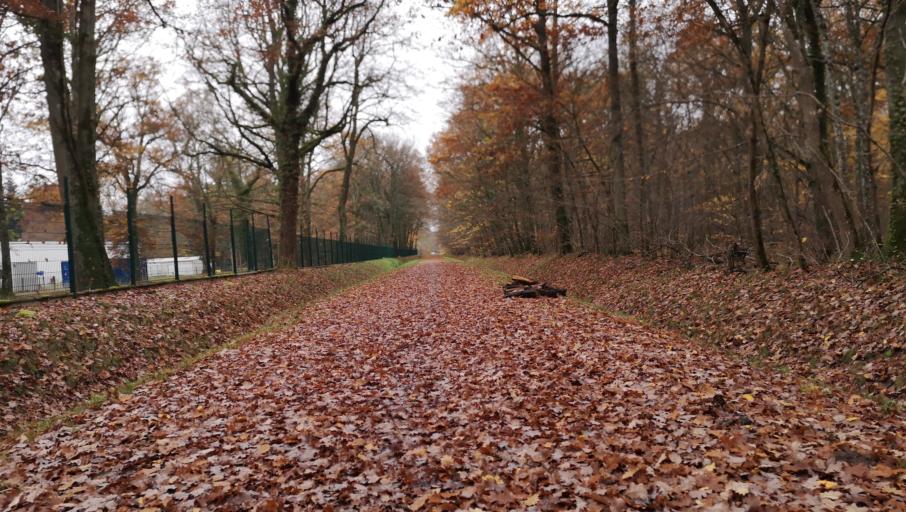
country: FR
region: Centre
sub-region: Departement du Loiret
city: Saint-Jean-de-Braye
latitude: 47.9282
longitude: 1.9865
